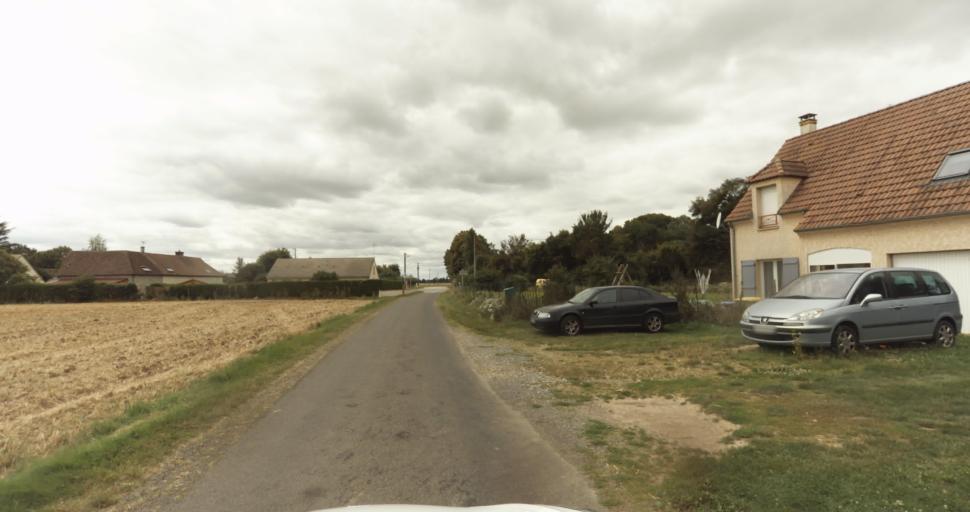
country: FR
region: Centre
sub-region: Departement d'Eure-et-Loir
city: Saint-Lubin-des-Joncherets
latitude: 48.8414
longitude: 1.2420
